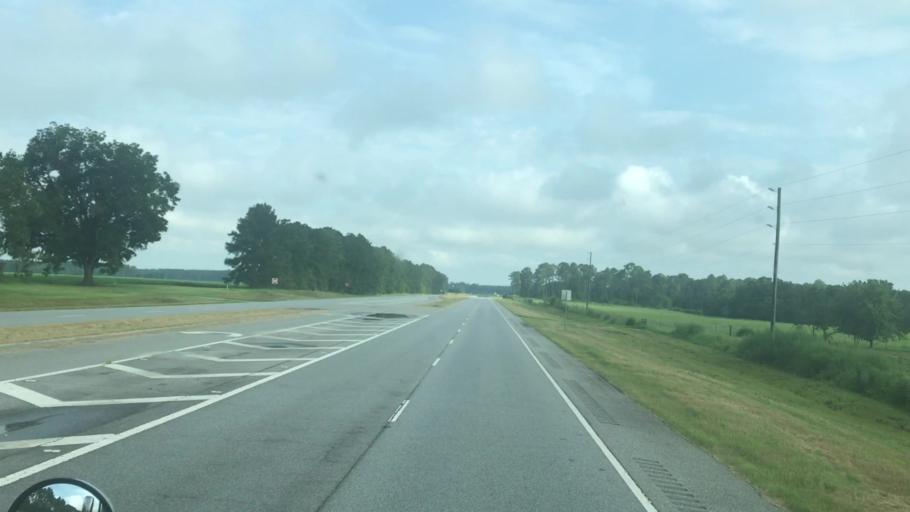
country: US
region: Georgia
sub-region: Miller County
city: Colquitt
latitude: 31.2082
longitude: -84.7730
